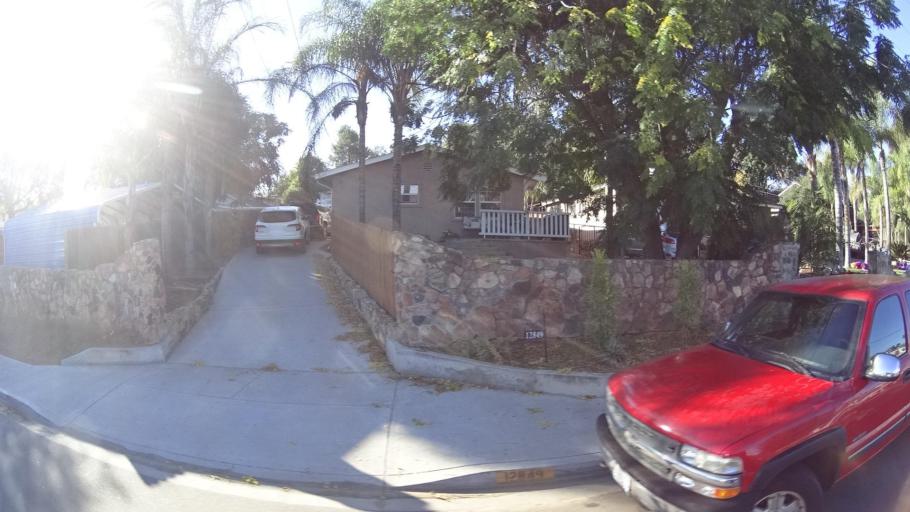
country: US
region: California
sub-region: San Diego County
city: Lakeside
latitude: 32.8560
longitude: -116.9143
